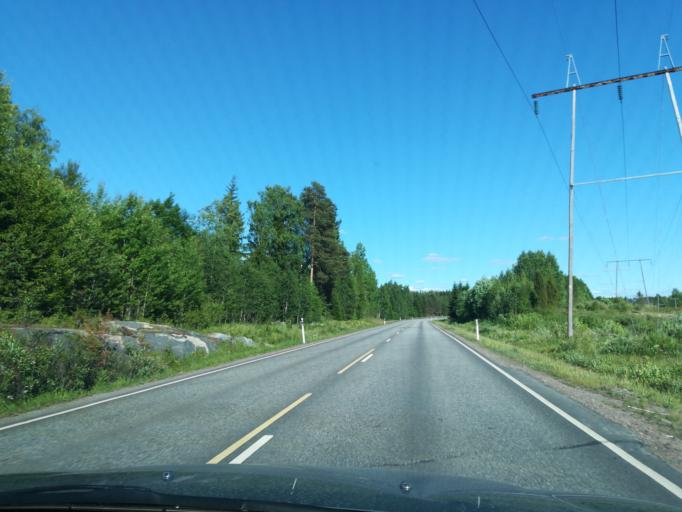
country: FI
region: South Karelia
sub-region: Imatra
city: Ruokolahti
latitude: 61.3500
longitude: 28.7532
